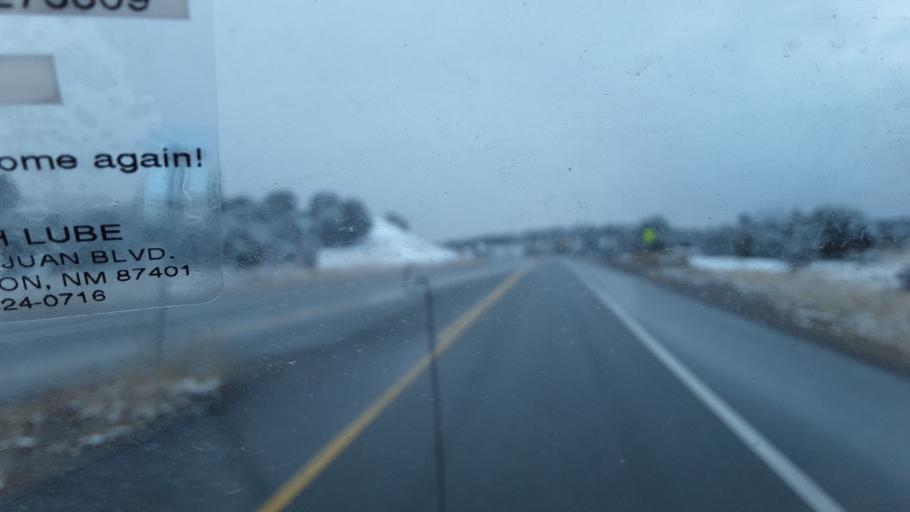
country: US
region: Colorado
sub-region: La Plata County
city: Bayfield
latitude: 37.2265
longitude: -107.6924
